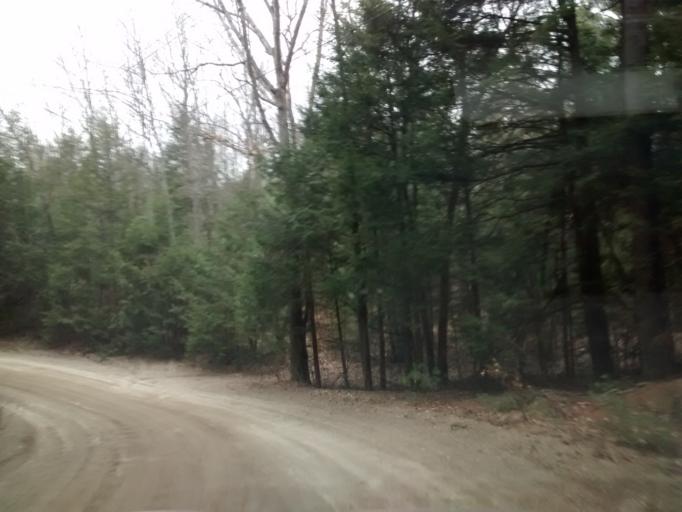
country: US
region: Massachusetts
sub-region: Franklin County
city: Orange
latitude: 42.5461
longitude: -72.2752
